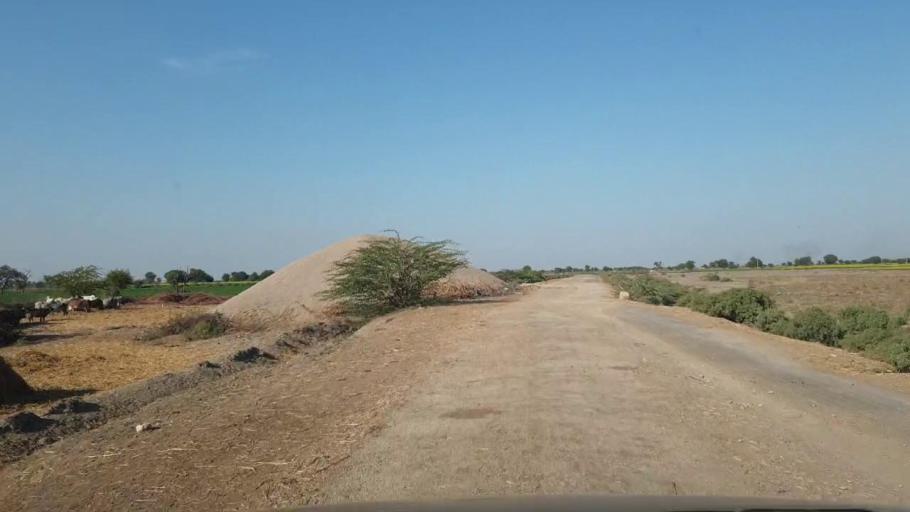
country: PK
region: Sindh
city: Khadro
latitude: 26.1624
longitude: 68.6861
